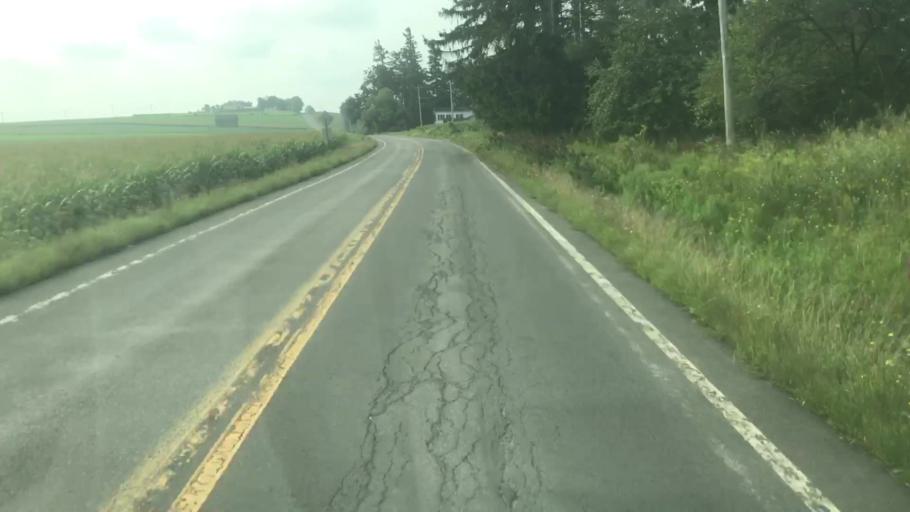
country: US
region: New York
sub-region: Onondaga County
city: Skaneateles
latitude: 42.8994
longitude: -76.4535
